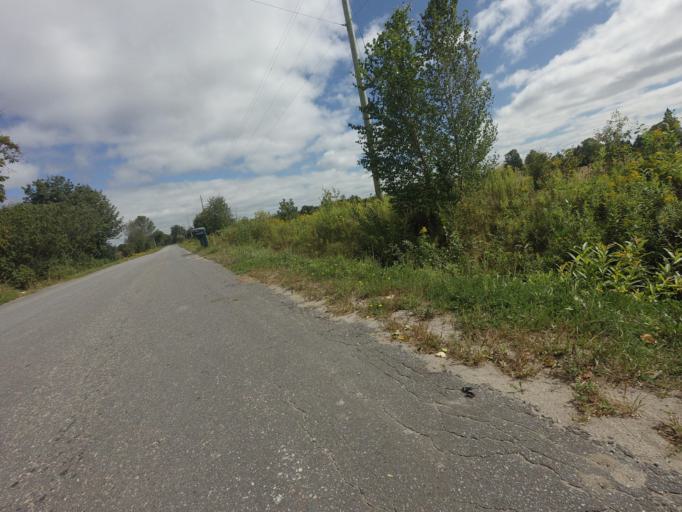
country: CA
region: Ontario
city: Uxbridge
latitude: 44.1273
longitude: -79.1264
